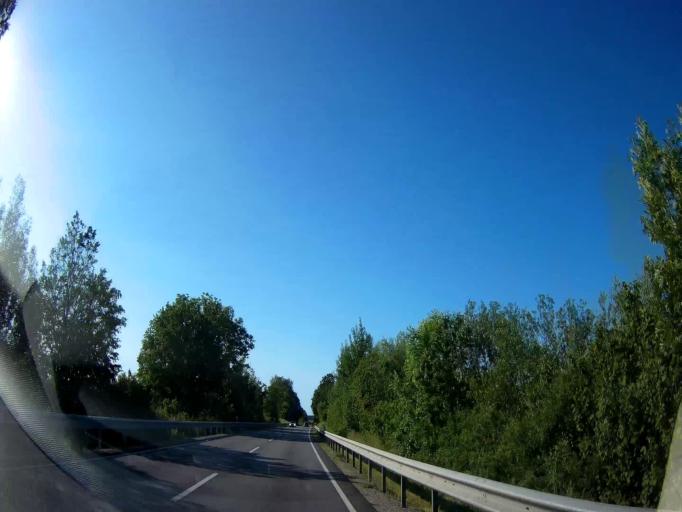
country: DE
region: Bavaria
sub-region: Lower Bavaria
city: Wurmannsquick
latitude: 48.3544
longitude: 12.7971
